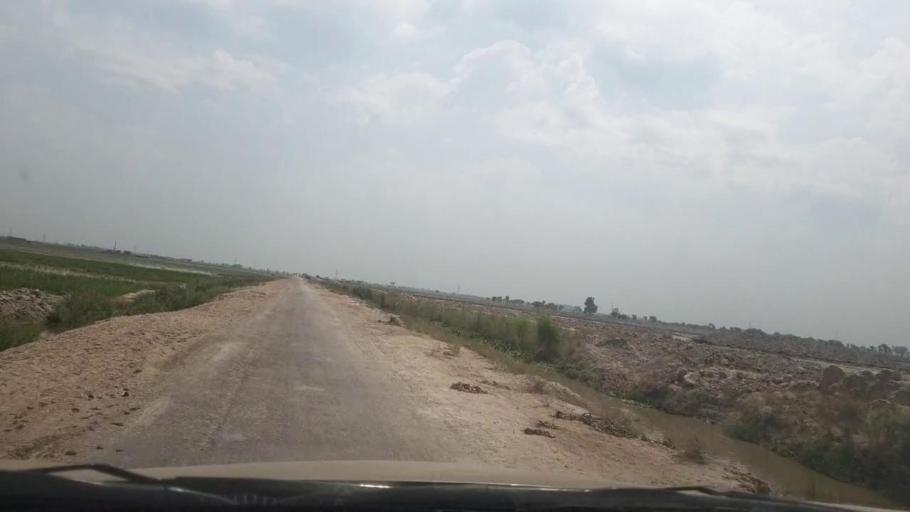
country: PK
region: Sindh
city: Ratodero
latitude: 27.7001
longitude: 68.2377
